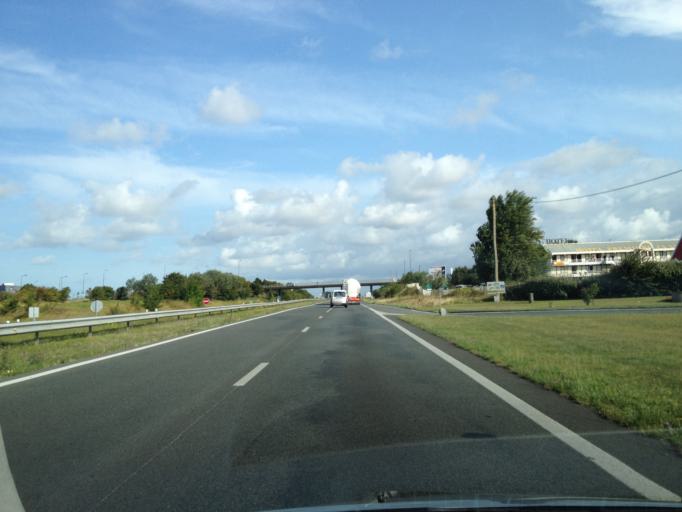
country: FR
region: Poitou-Charentes
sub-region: Departement de la Charente-Maritime
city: Angoulins
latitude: 46.1021
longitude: -1.0938
